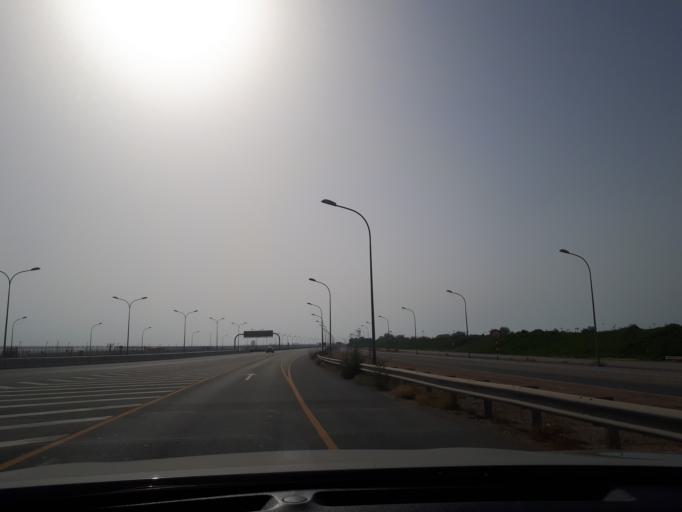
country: OM
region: Muhafazat Masqat
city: Bawshar
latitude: 23.6099
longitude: 58.3070
